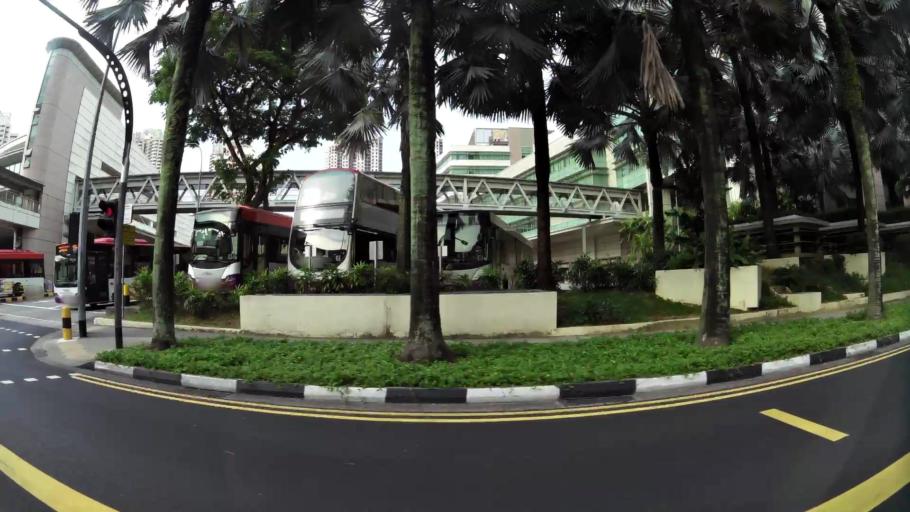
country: SG
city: Singapore
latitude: 1.3314
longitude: 103.8480
